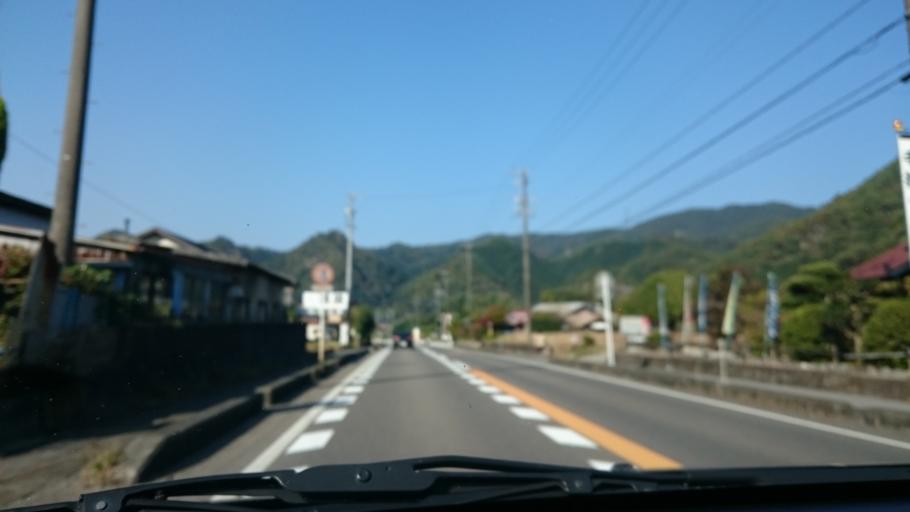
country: JP
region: Gifu
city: Minokamo
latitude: 35.5210
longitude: 137.1051
